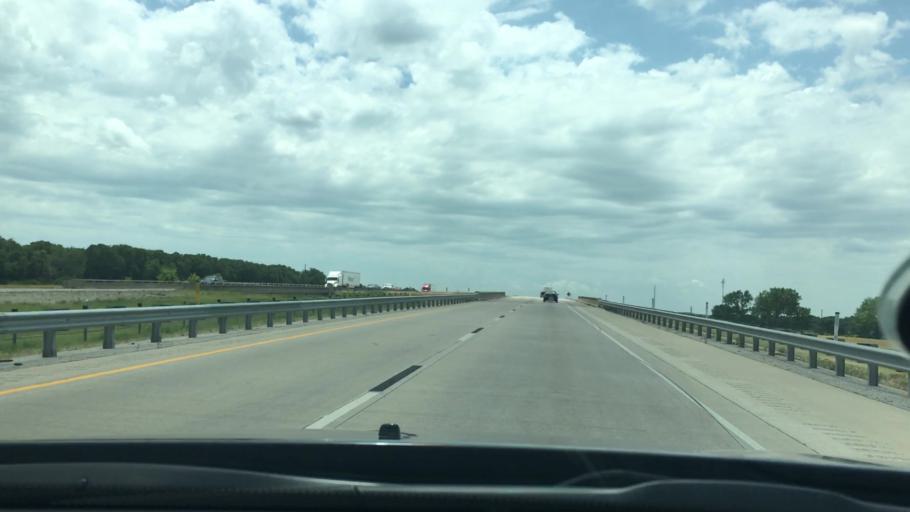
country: US
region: Oklahoma
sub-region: Carter County
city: Ardmore
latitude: 34.1404
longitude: -97.1558
